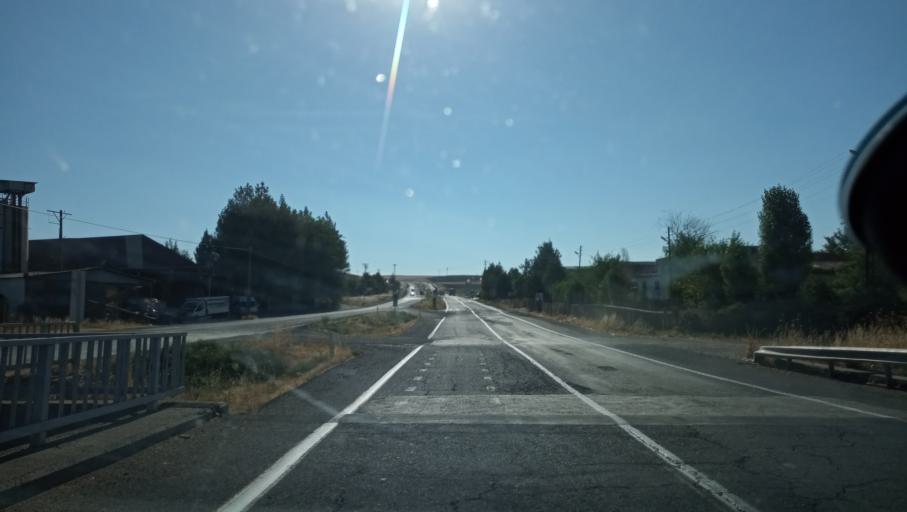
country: TR
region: Diyarbakir
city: Sur
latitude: 37.9909
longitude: 40.3839
